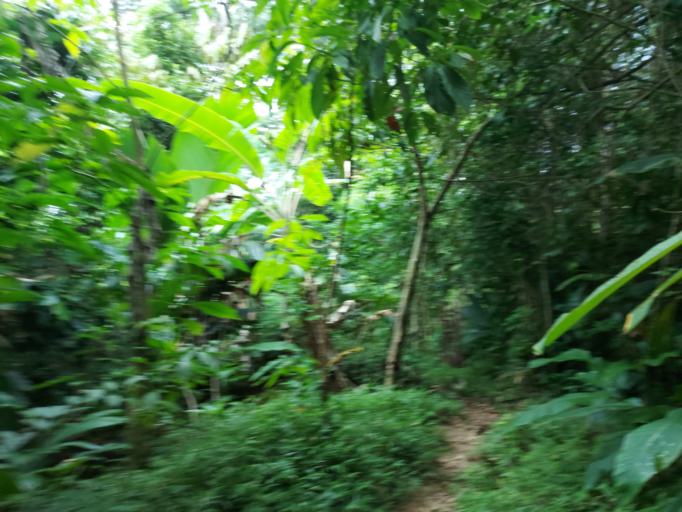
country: PA
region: Bocas del Toro
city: Barranco
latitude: 9.6389
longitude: -82.7820
